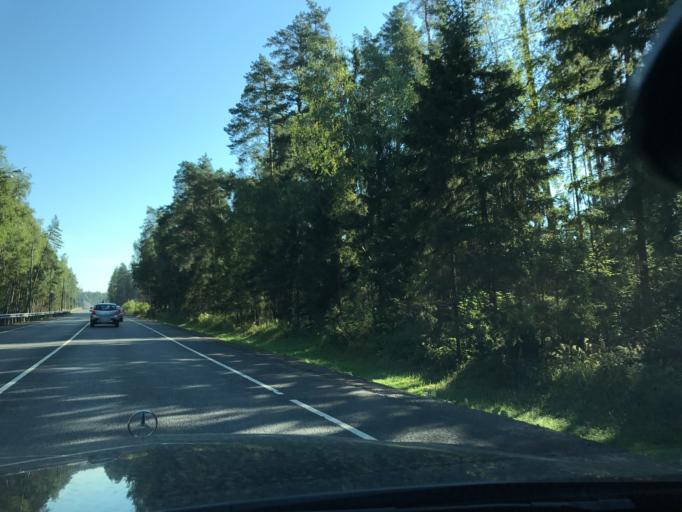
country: RU
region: Moskovskaya
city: Chernogolovka
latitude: 55.9722
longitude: 38.2978
